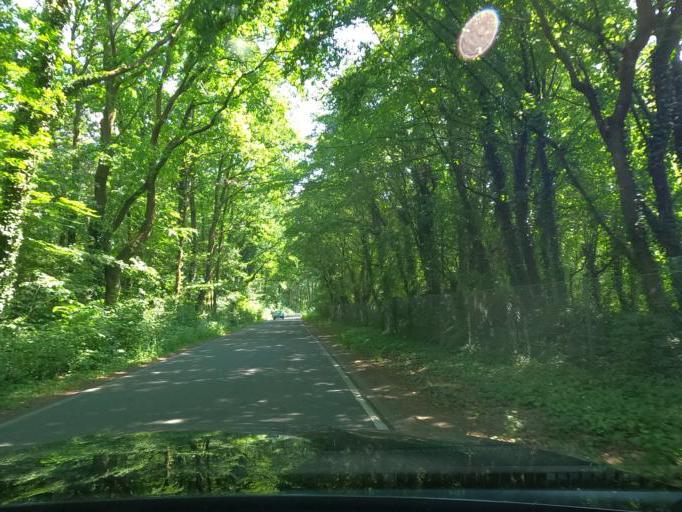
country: DE
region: Lower Saxony
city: Isernhagen Farster Bauerschaft
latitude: 52.4024
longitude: 9.8570
